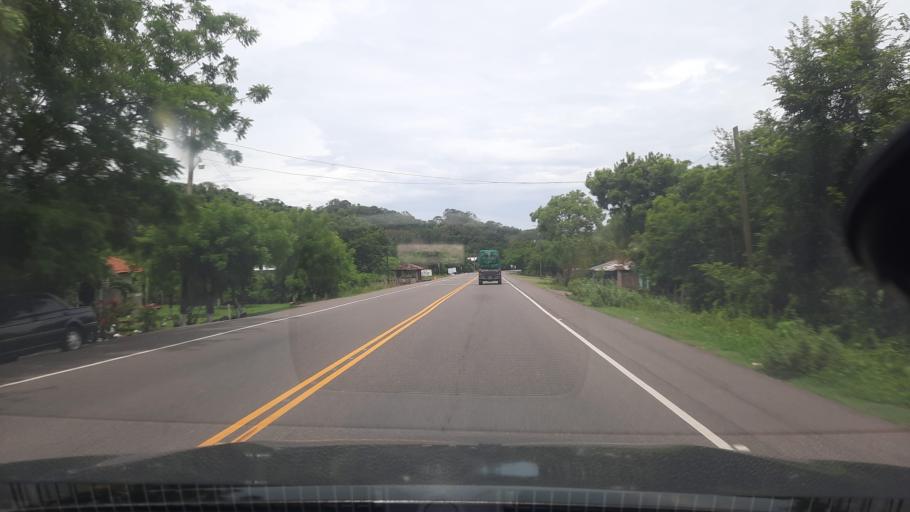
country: HN
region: Valle
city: Goascoran
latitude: 13.5621
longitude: -87.6619
